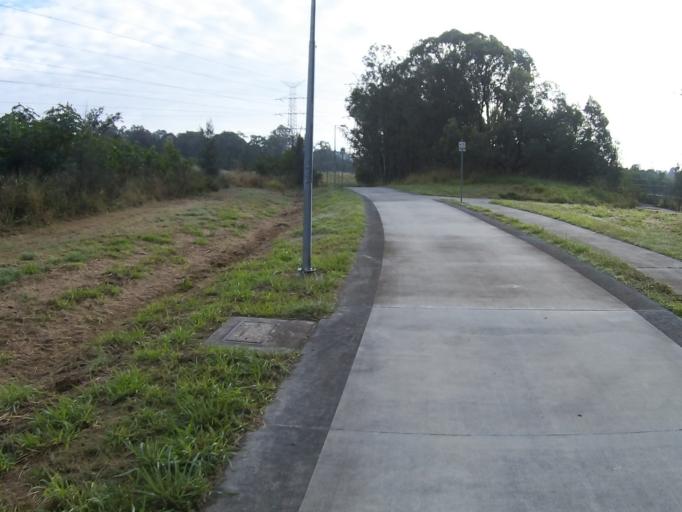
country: AU
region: Queensland
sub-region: Logan
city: Rochedale South
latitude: -27.5834
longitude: 153.1010
